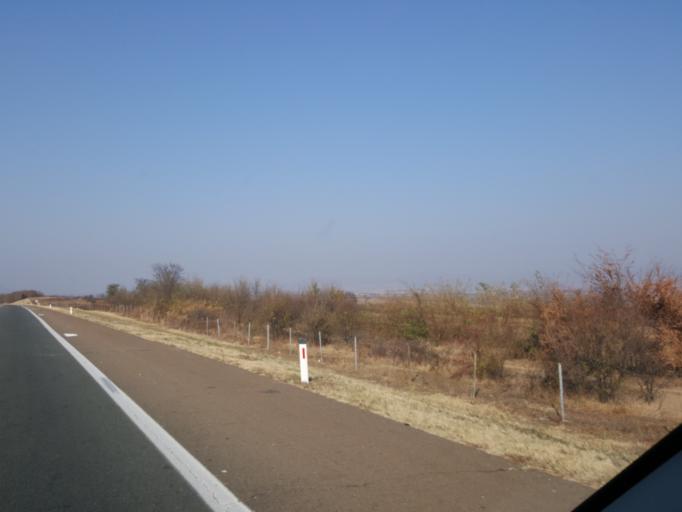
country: RS
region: Central Serbia
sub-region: Nisavski Okrug
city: Doljevac
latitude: 43.2587
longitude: 21.8131
